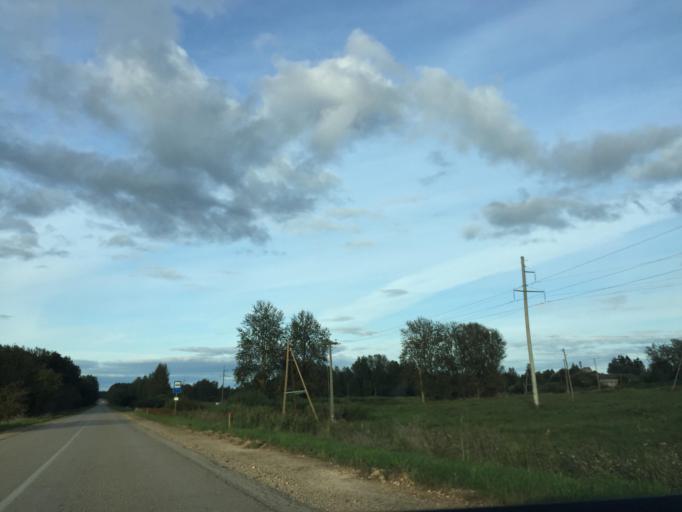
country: LV
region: Nereta
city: Nereta
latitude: 56.2777
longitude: 25.3902
